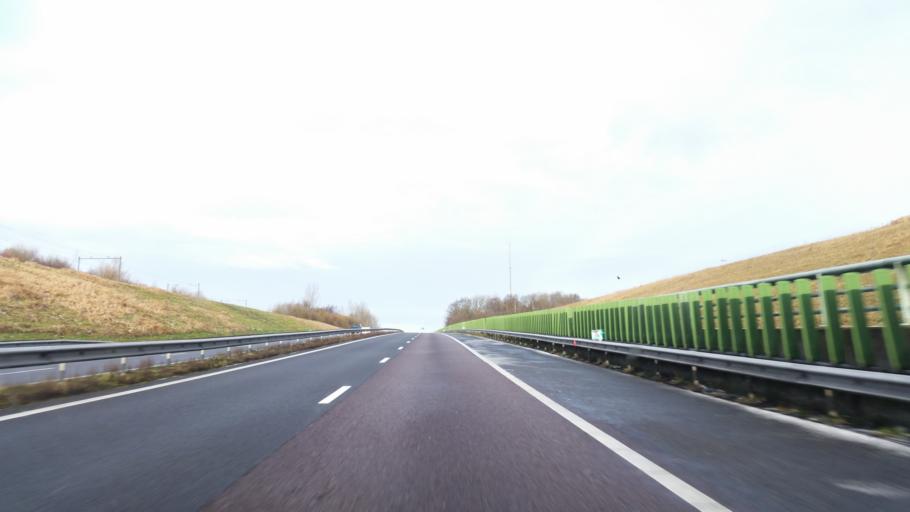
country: NL
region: Friesland
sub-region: Gemeente Boarnsterhim
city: Grou
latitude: 53.0798
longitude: 5.8289
